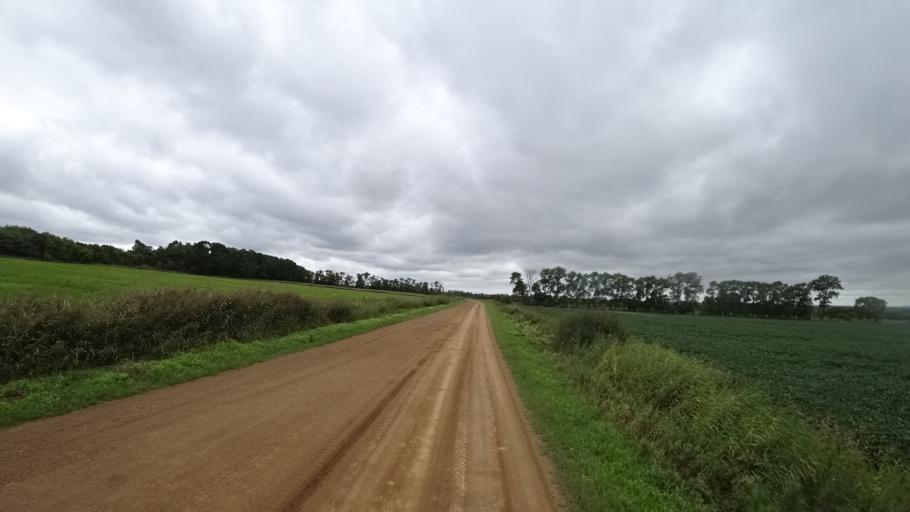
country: RU
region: Primorskiy
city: Chernigovka
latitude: 44.4506
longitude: 132.5775
